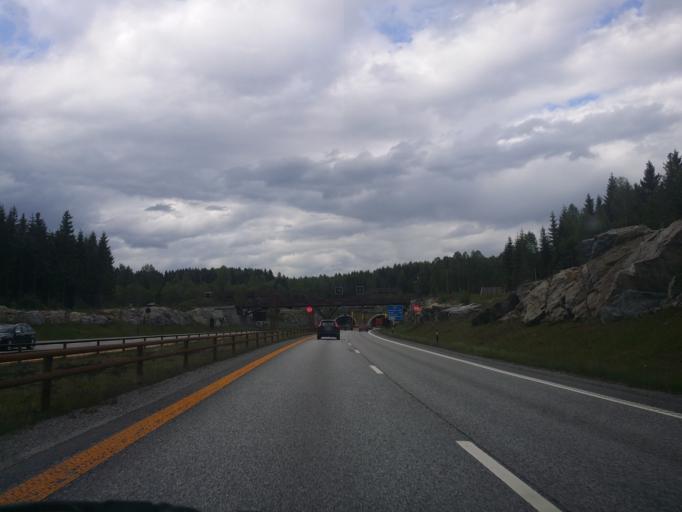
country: NO
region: Akershus
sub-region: Eidsvoll
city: Raholt
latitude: 60.3345
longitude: 11.1929
